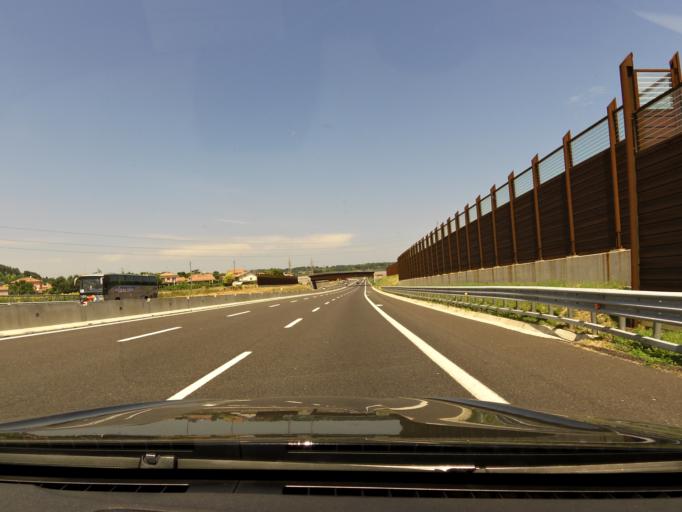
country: IT
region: The Marches
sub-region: Provincia di Pesaro e Urbino
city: Rosciano
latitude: 43.8256
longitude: 12.9977
